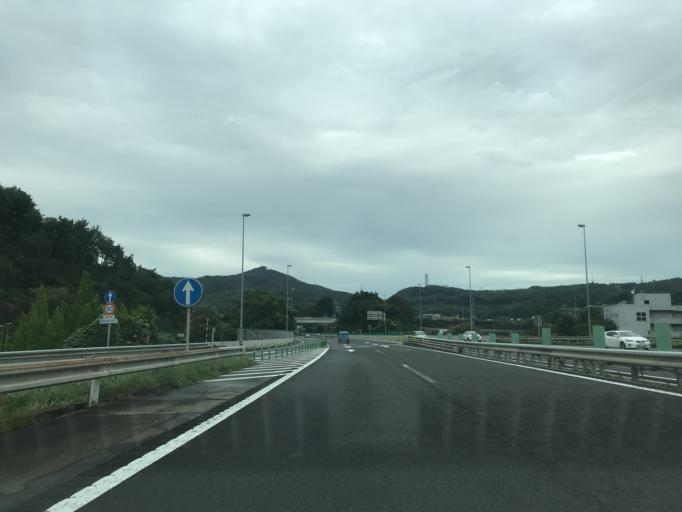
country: JP
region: Miyagi
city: Sendai
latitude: 38.2589
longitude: 140.8108
